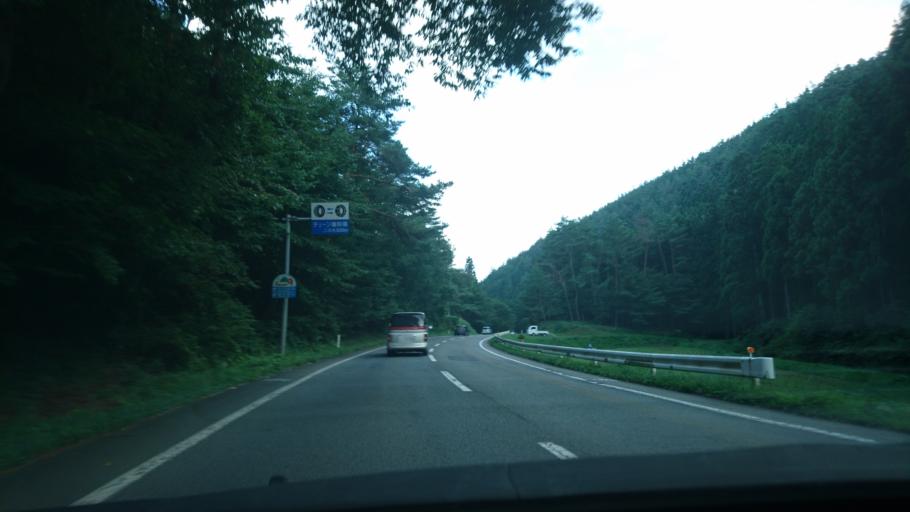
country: JP
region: Iwate
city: Mizusawa
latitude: 39.0479
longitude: 141.2327
